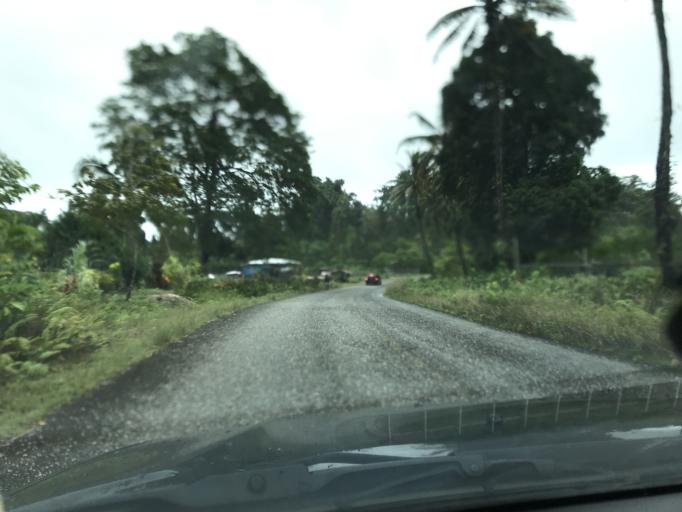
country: SB
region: Western Province
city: Gizo
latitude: -8.2491
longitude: 157.2361
